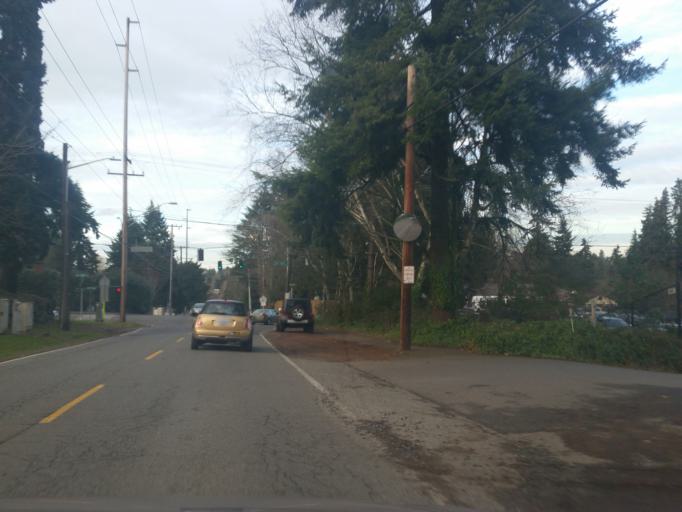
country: US
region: Washington
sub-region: King County
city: Shoreline
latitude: 47.7334
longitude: -122.3289
